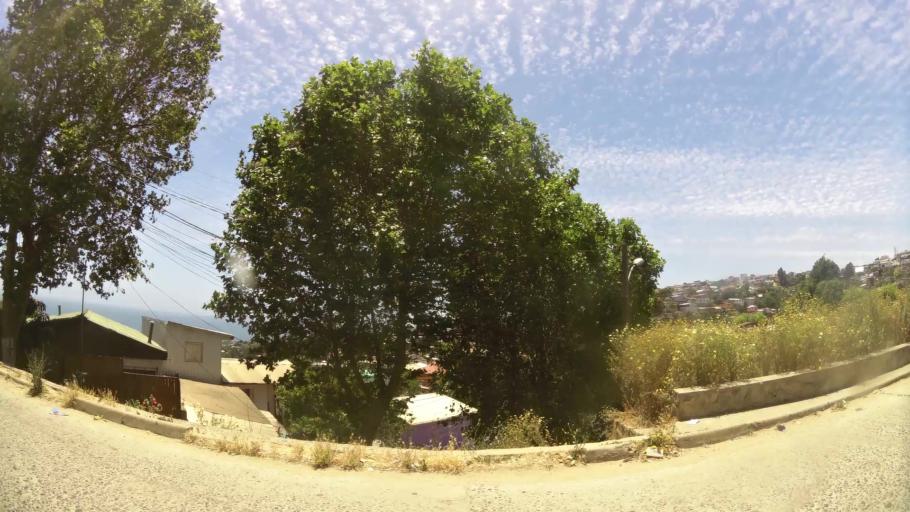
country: CL
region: Valparaiso
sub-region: Provincia de Valparaiso
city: Vina del Mar
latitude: -33.0431
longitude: -71.5846
